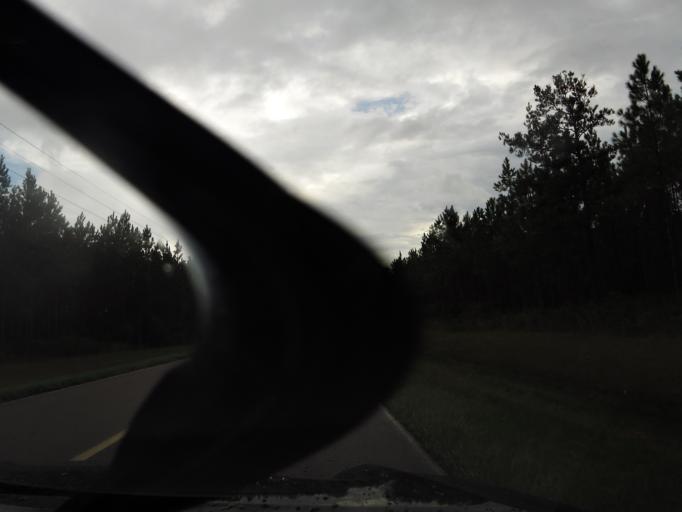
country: US
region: Florida
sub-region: Nassau County
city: Callahan
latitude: 30.5191
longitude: -81.9928
